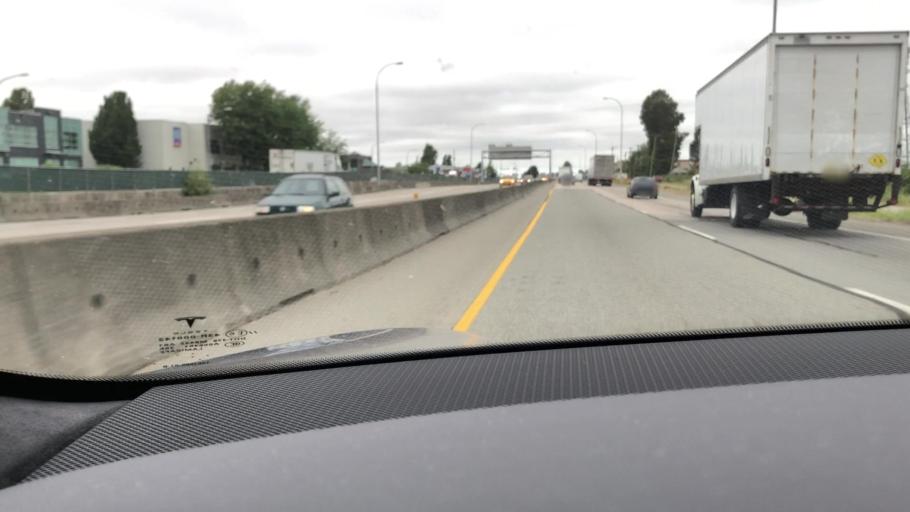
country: CA
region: British Columbia
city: Delta
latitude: 49.1698
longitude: -122.9841
